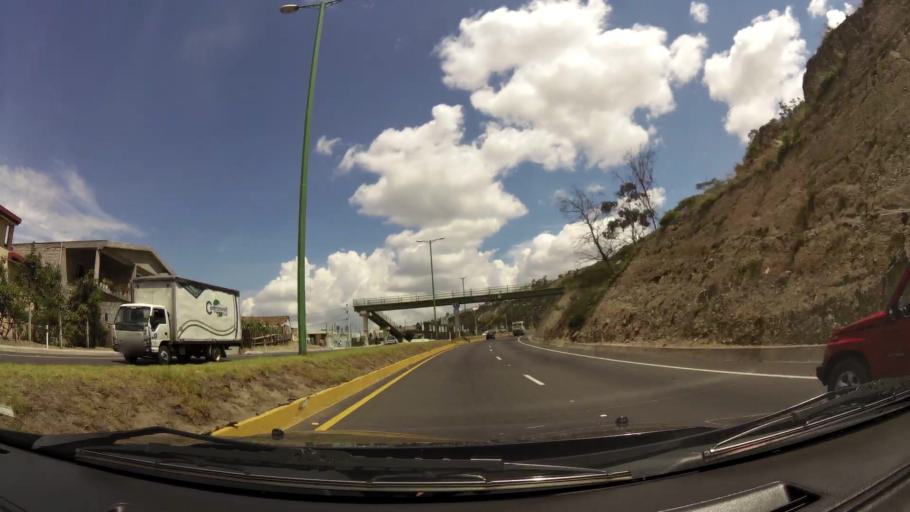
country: EC
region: Pichincha
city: Quito
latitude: -0.0919
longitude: -78.4123
